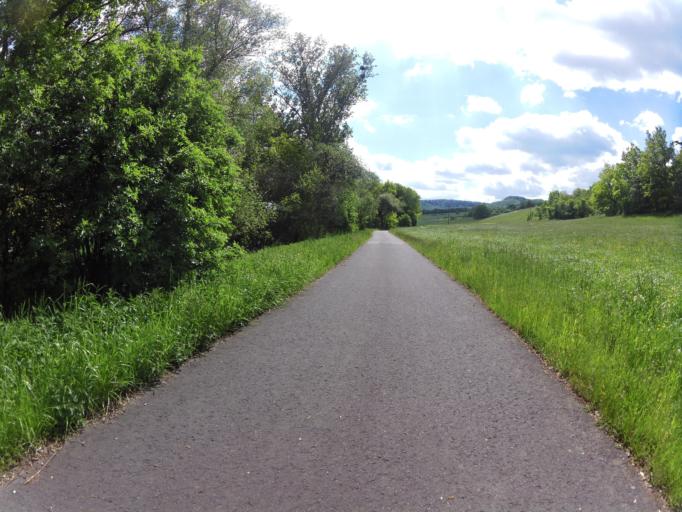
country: DE
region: Thuringia
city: Treffurt
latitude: 51.1199
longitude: 10.2313
